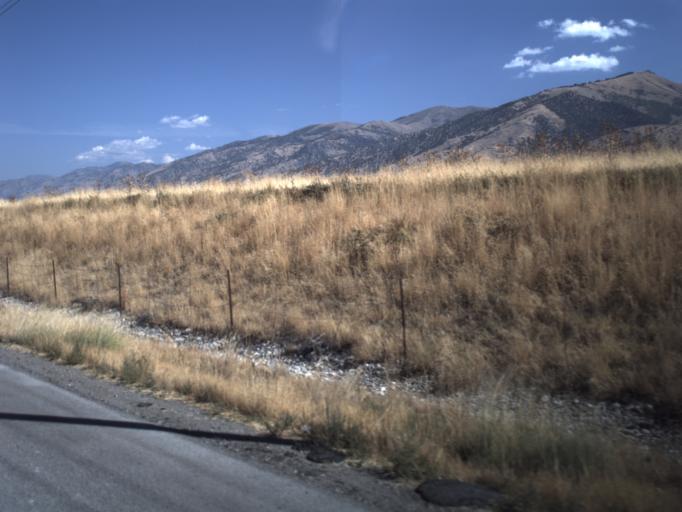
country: US
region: Utah
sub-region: Cache County
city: Hyrum
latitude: 41.6425
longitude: -111.8326
